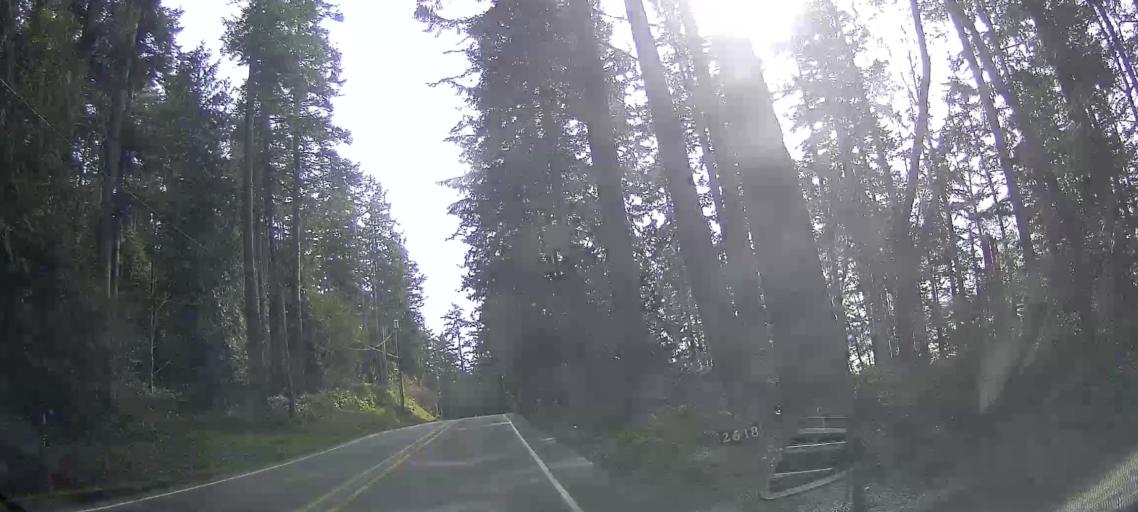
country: US
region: Washington
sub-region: Island County
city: Langley
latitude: 48.1157
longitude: -122.4489
